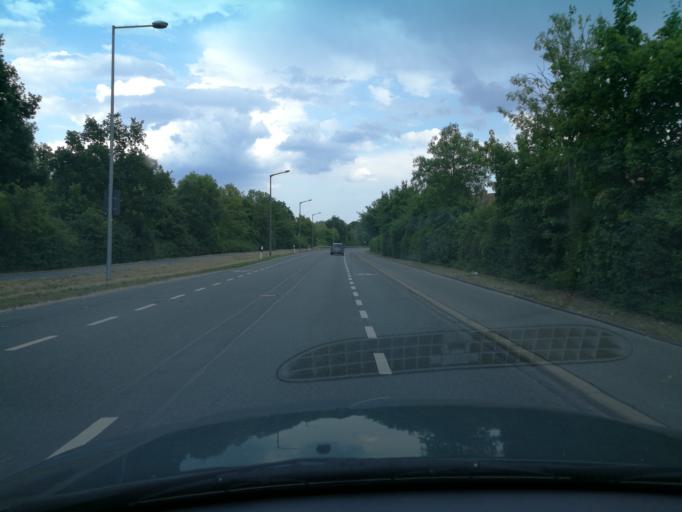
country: DE
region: Bavaria
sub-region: Regierungsbezirk Mittelfranken
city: Zirndorf
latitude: 49.4666
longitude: 10.9547
